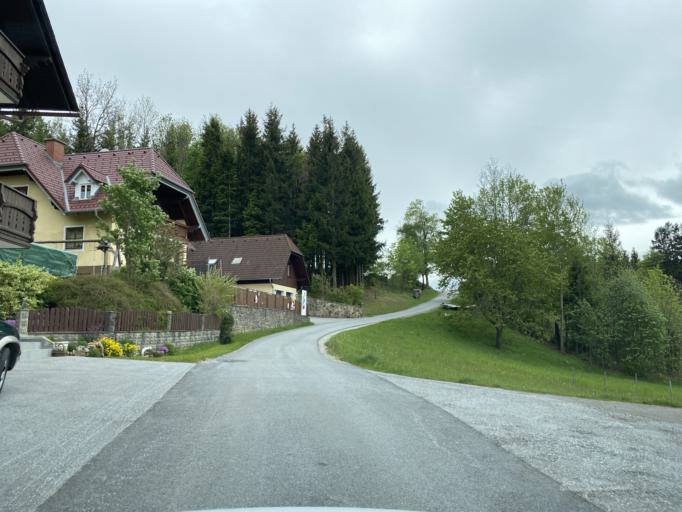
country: AT
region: Styria
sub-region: Politischer Bezirk Weiz
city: Koglhof
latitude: 47.3138
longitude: 15.7059
